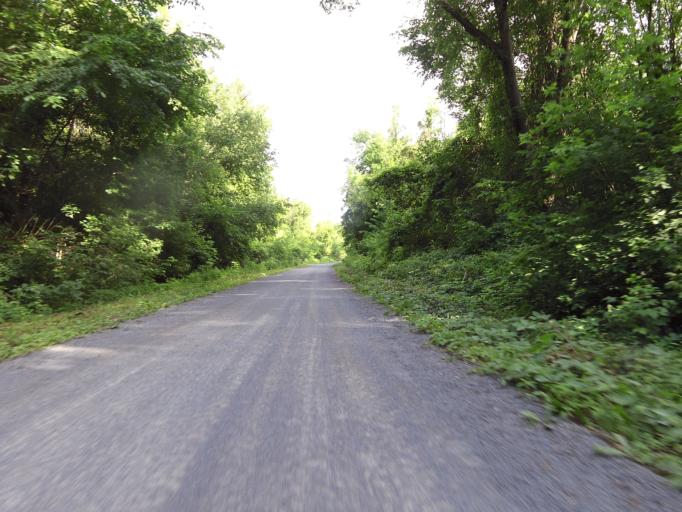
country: CA
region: Ontario
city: Arnprior
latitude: 45.3245
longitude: -76.2879
